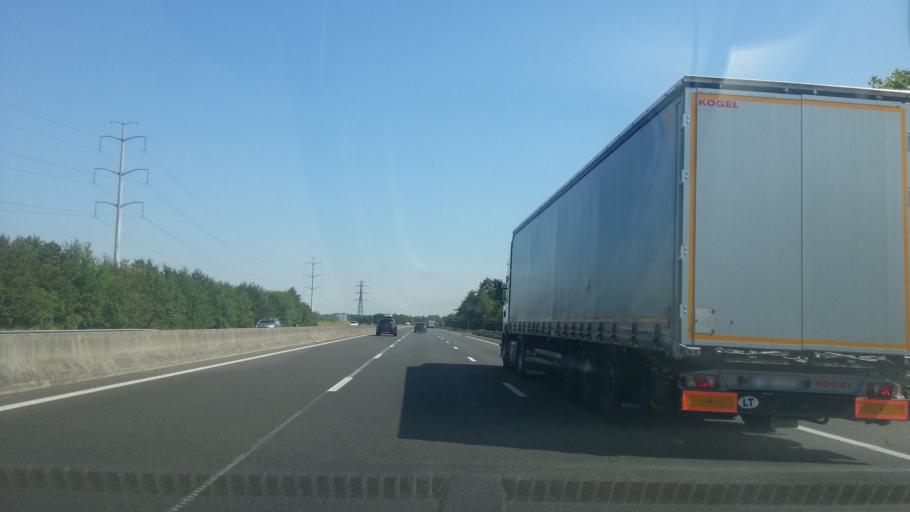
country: FR
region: Centre
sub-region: Departement du Loiret
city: Meung-sur-Loire
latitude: 47.8409
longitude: 1.6749
